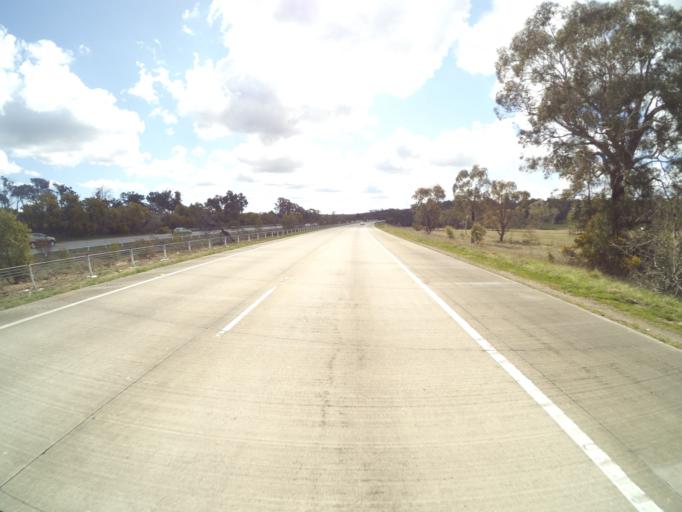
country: AU
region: New South Wales
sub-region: Wingecarribee
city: Moss Vale
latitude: -34.4872
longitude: 150.3123
